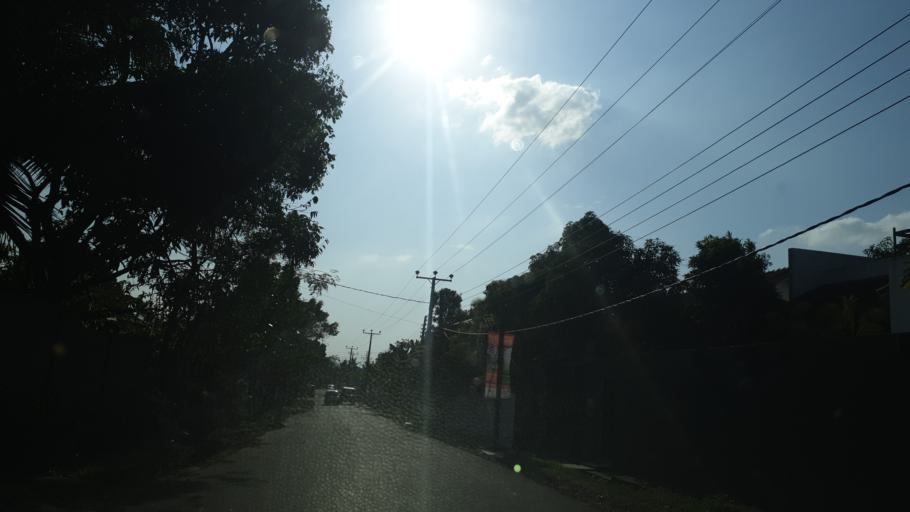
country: LK
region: Western
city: Battaramulla South
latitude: 6.8833
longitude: 79.9401
